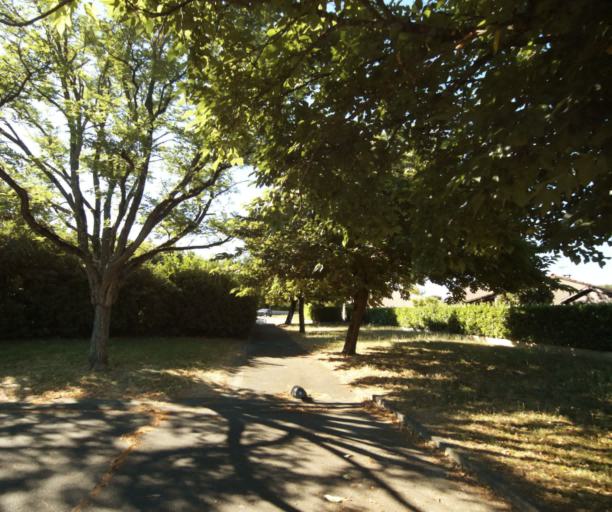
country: FR
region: Midi-Pyrenees
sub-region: Departement de la Haute-Garonne
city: Castanet-Tolosan
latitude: 43.5239
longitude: 1.5116
